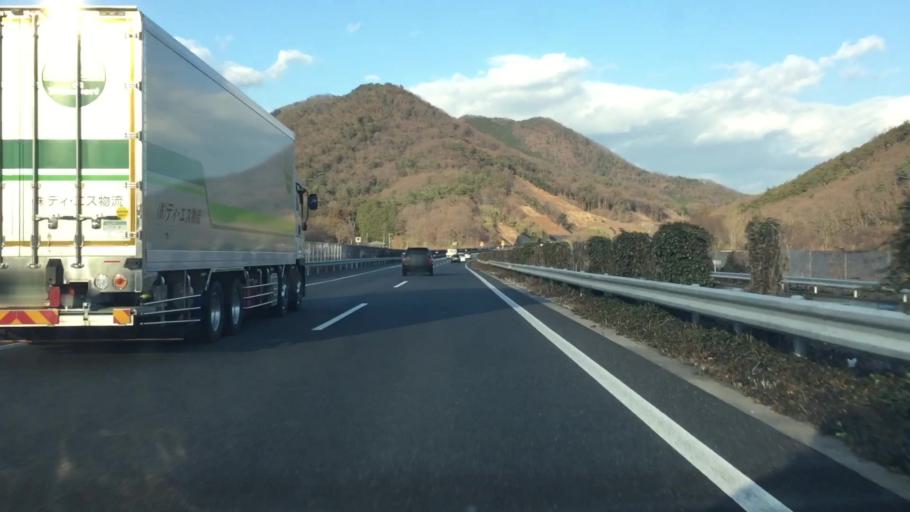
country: JP
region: Tochigi
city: Ashikaga
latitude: 36.3521
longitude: 139.4205
